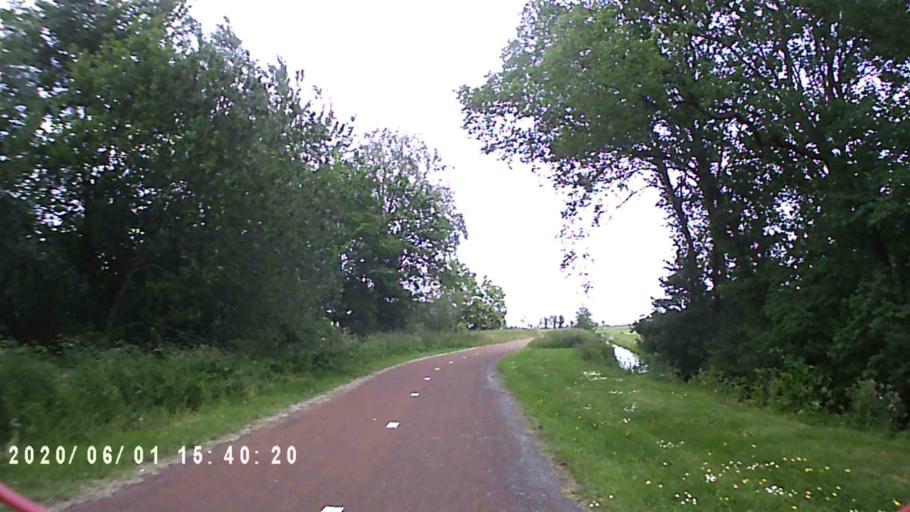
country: NL
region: Friesland
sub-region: Gemeente Leeuwarden
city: Wirdum
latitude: 53.1535
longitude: 5.8211
